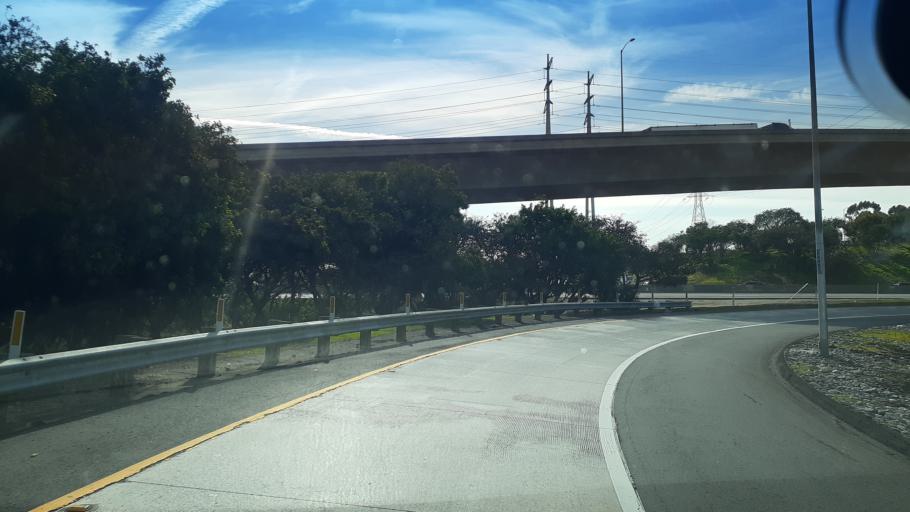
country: US
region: California
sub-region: Los Angeles County
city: West Rancho Dominguez
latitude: 33.8736
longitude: -118.2835
